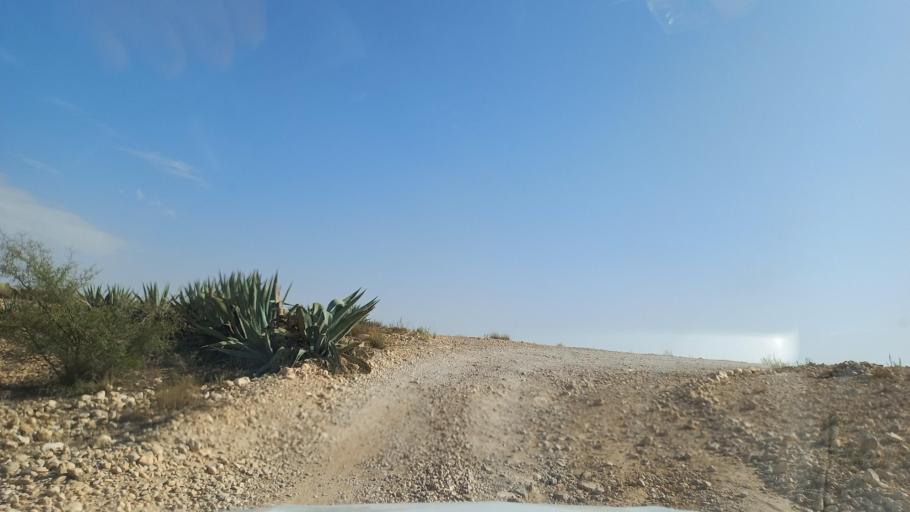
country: TN
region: Al Qasrayn
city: Kasserine
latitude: 35.2610
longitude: 8.9268
